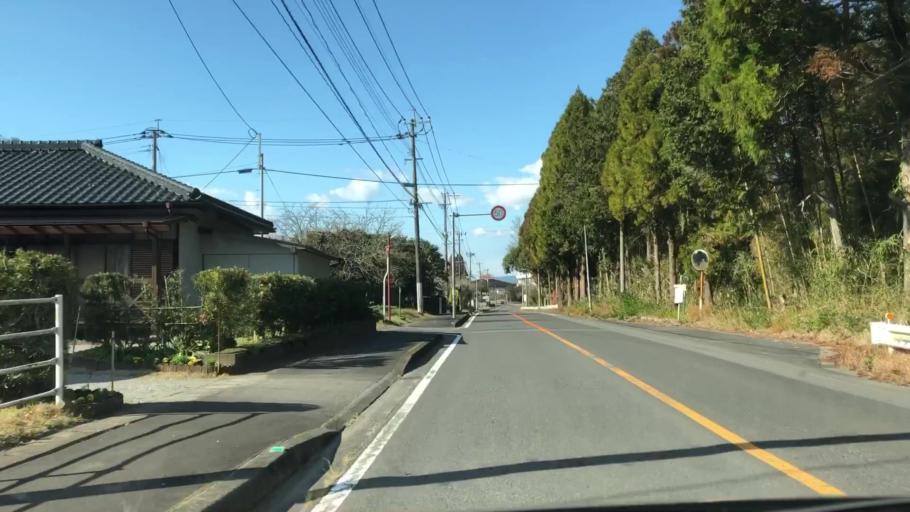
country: JP
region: Kagoshima
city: Satsumasendai
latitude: 31.7989
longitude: 130.4392
